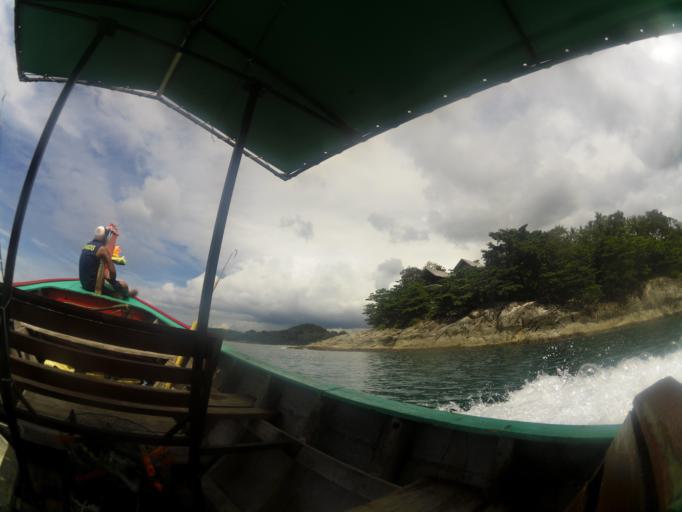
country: TH
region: Phuket
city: Patong
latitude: 7.9695
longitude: 98.2764
